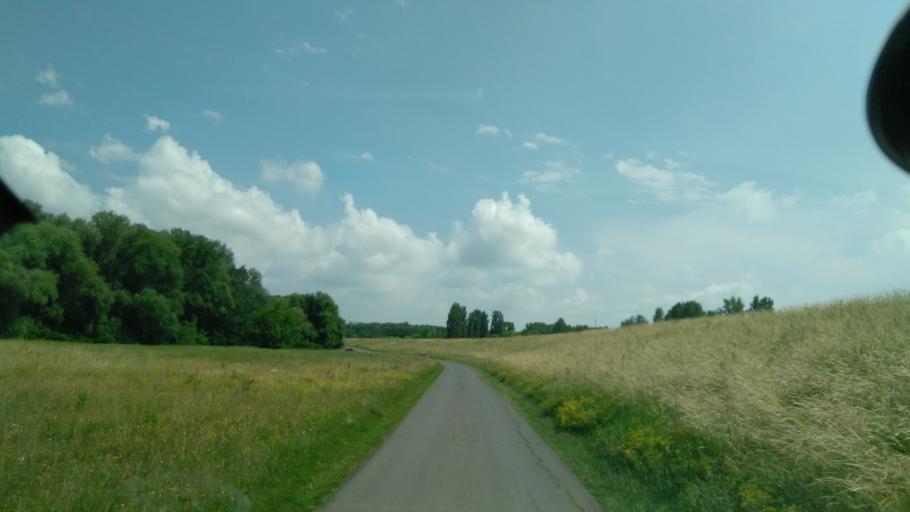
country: HU
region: Bekes
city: Bekes
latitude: 46.7626
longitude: 21.1512
